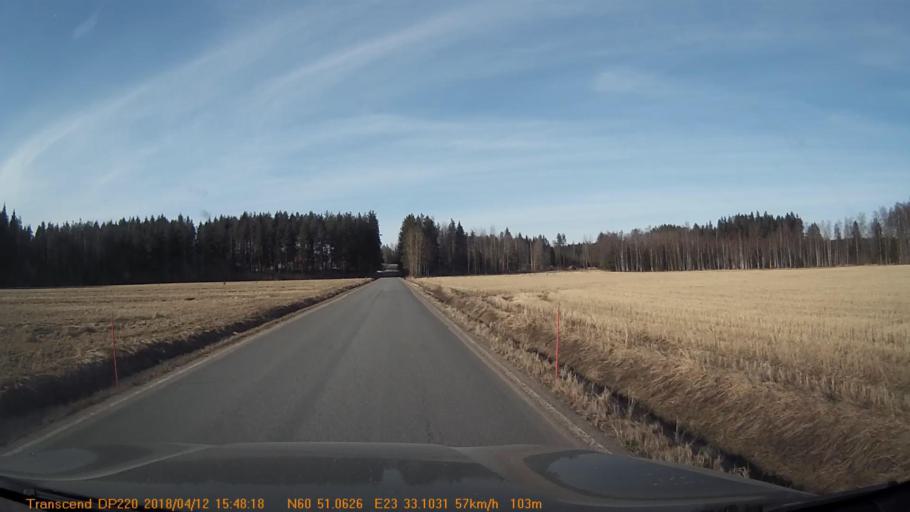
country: FI
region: Haeme
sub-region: Forssa
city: Forssa
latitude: 60.8513
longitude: 23.5515
